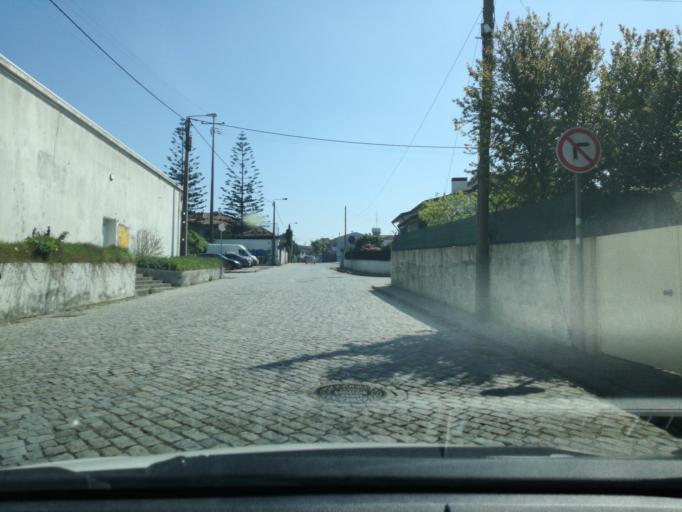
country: PT
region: Porto
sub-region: Maia
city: Gemunde
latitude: 41.2492
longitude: -8.6654
